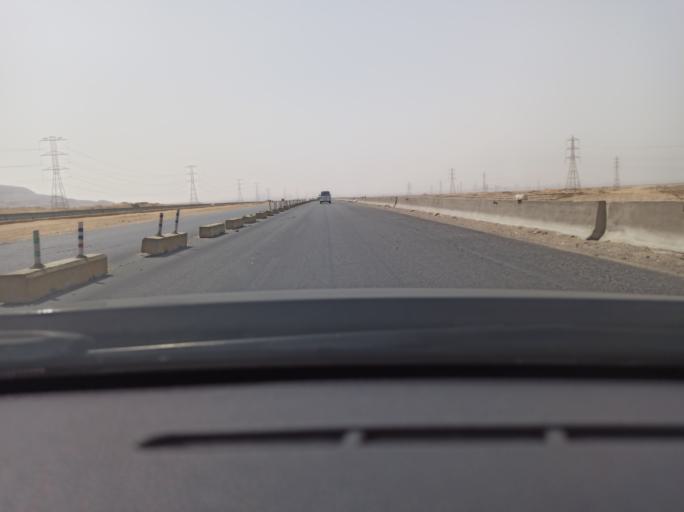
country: EG
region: Muhafazat Bani Suwayf
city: Bush
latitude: 29.1117
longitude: 31.2186
